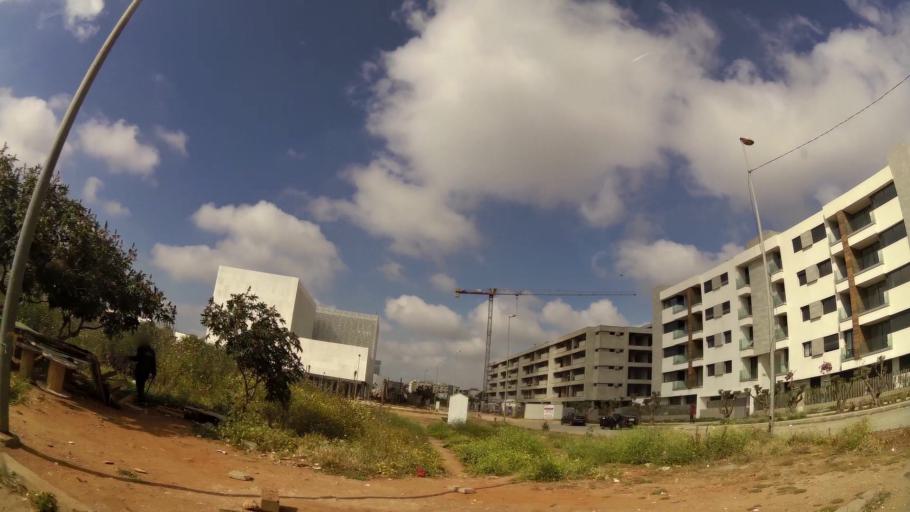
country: MA
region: Rabat-Sale-Zemmour-Zaer
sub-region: Skhirate-Temara
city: Temara
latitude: 33.9501
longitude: -6.8787
